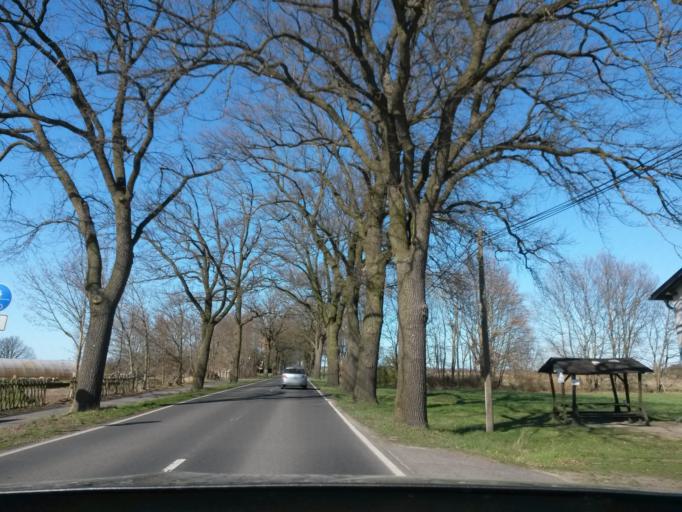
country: DE
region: Brandenburg
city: Rehfelde
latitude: 52.5079
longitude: 13.9302
